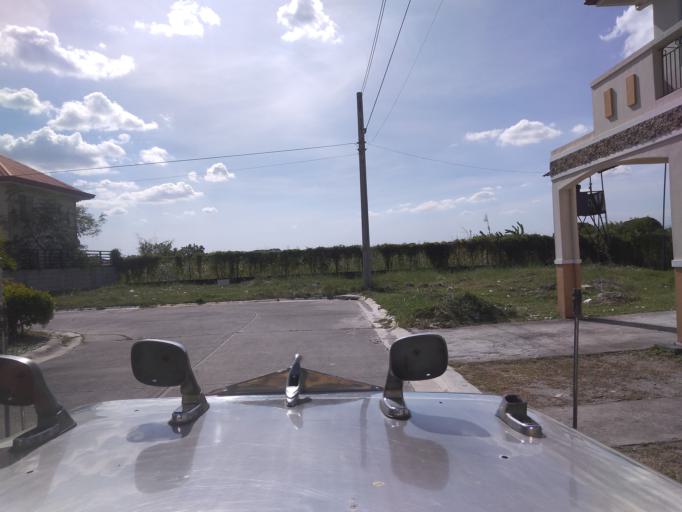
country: PH
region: Central Luzon
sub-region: Province of Pampanga
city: Magliman
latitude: 15.0244
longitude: 120.6591
